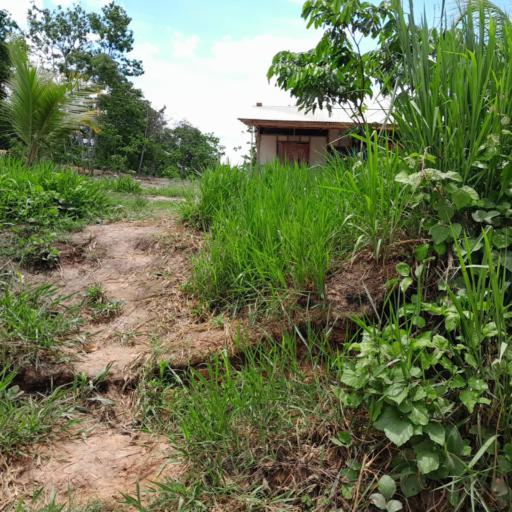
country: PE
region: Ucayali
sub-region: Provincia de Coronel Portillo
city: Puerto Callao
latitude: -8.2723
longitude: -74.6476
